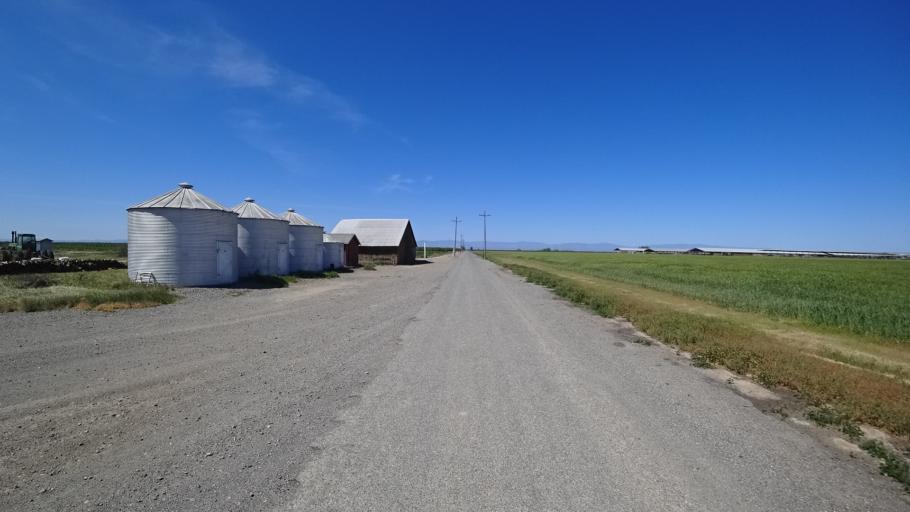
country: US
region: California
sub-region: Glenn County
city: Orland
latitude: 39.6382
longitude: -122.1240
